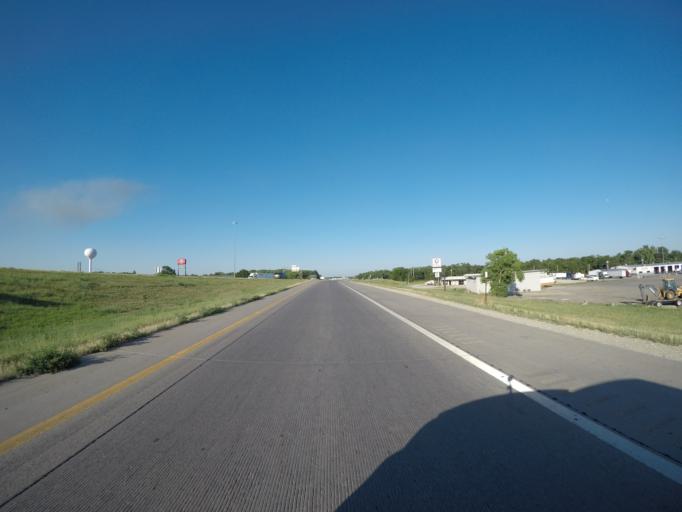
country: US
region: Kansas
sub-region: Saline County
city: Salina
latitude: 38.8761
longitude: -97.6105
